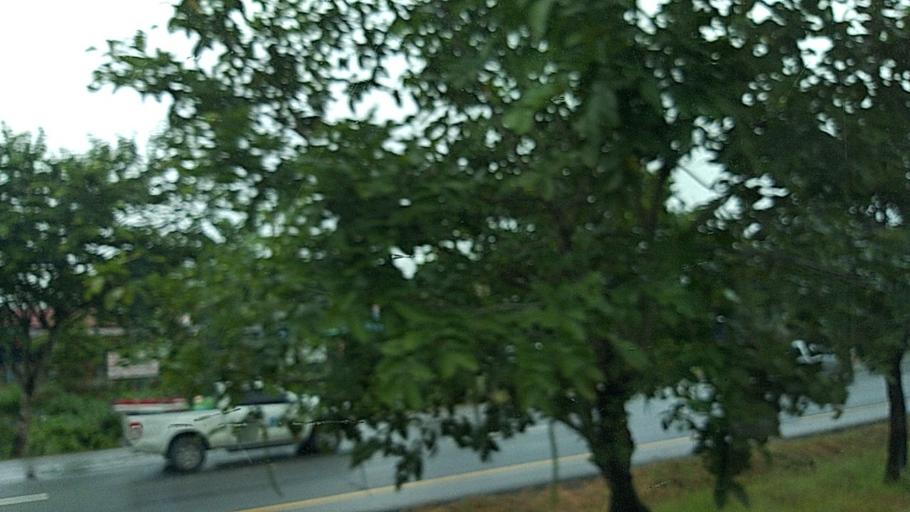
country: TH
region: Nakhon Ratchasima
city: Non Sung
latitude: 15.2192
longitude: 102.3607
